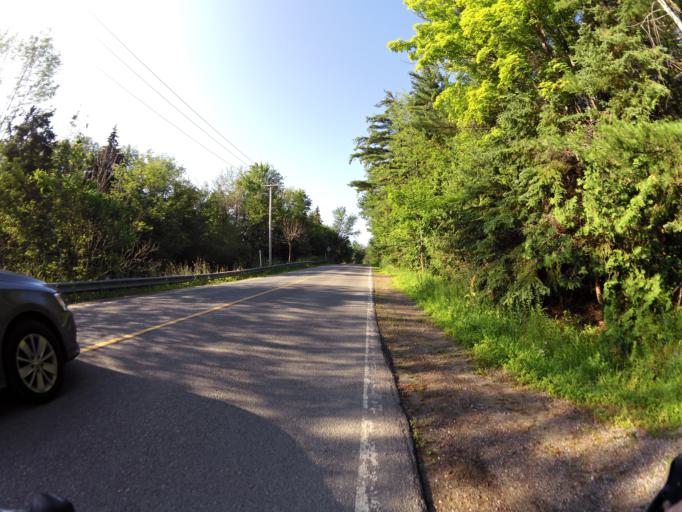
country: CA
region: Quebec
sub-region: Outaouais
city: Wakefield
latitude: 45.5786
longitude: -75.8716
